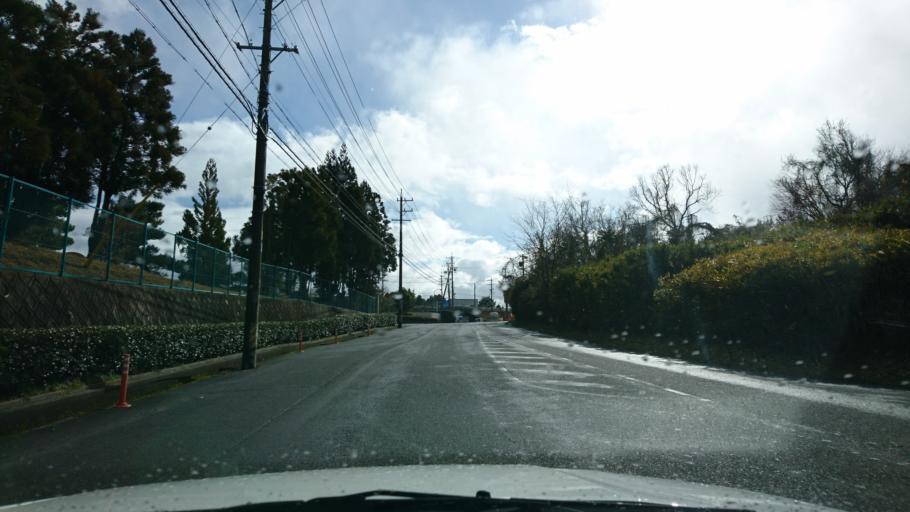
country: JP
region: Mie
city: Ueno-ebisumachi
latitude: 34.7249
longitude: 136.0845
